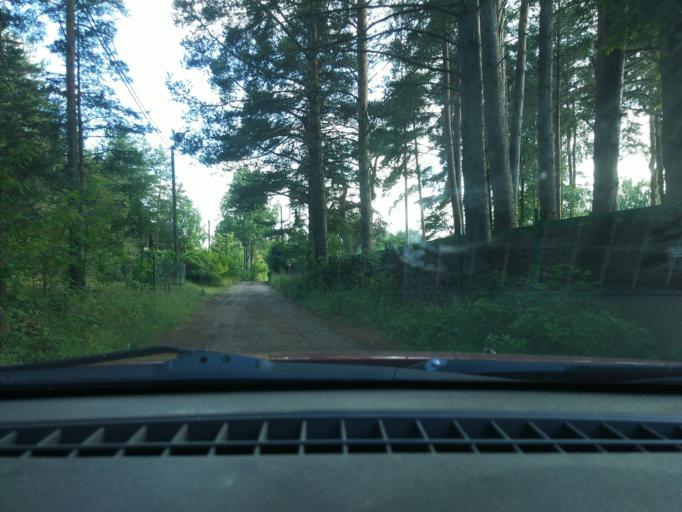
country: RU
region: Leningrad
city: Priozersk
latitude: 60.9405
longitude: 30.0452
